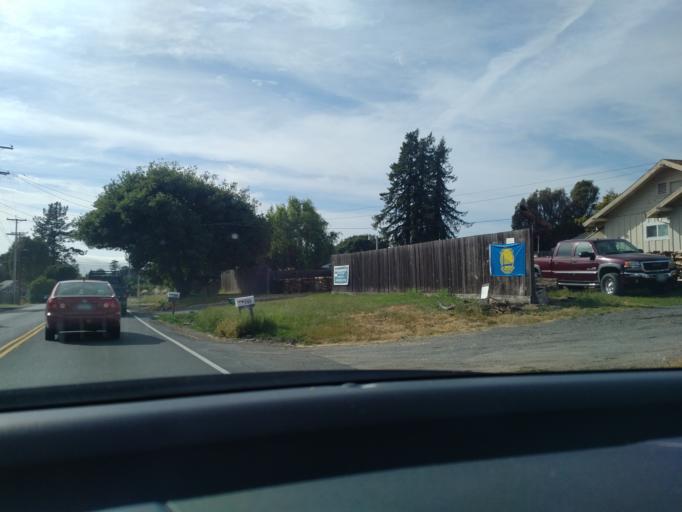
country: US
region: California
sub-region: Sonoma County
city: Penngrove
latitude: 38.2966
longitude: -122.6584
